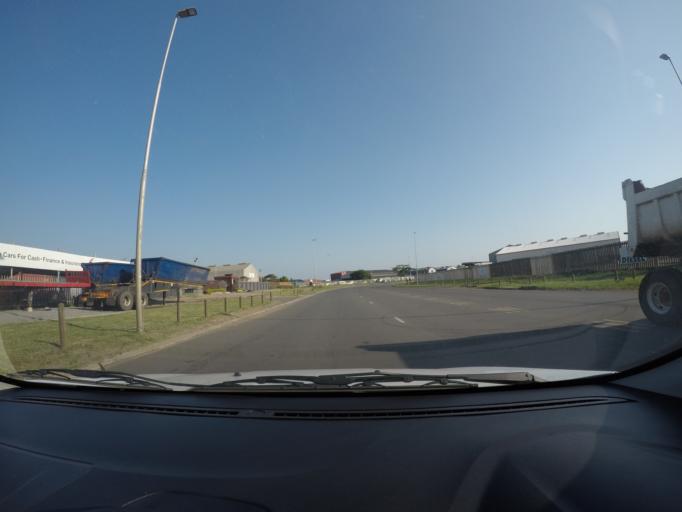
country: ZA
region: KwaZulu-Natal
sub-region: uThungulu District Municipality
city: Richards Bay
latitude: -28.7366
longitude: 32.0372
